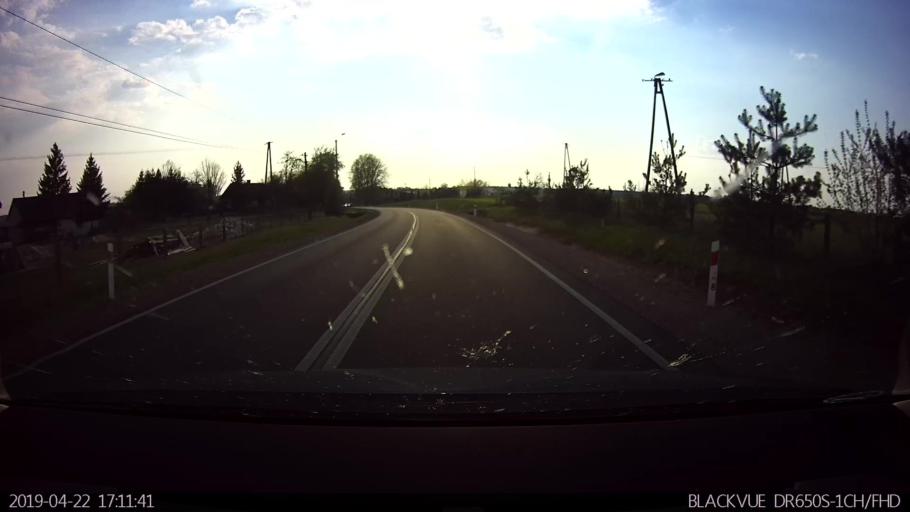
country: PL
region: Masovian Voivodeship
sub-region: Powiat siedlecki
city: Korczew
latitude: 52.4115
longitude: 22.5489
